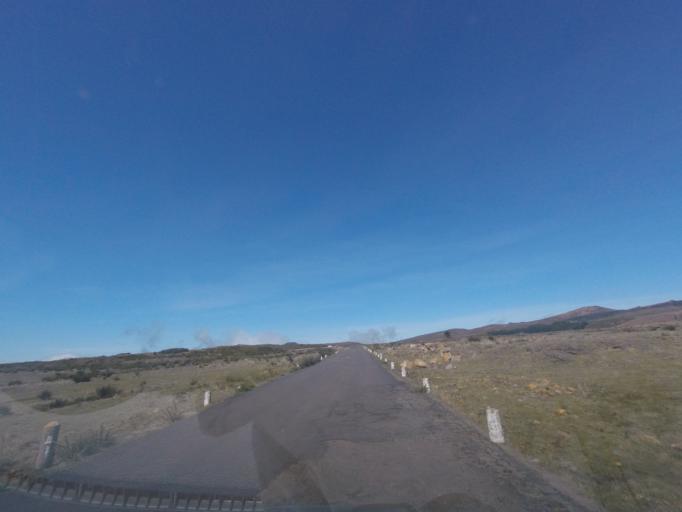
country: PT
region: Madeira
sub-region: Calheta
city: Arco da Calheta
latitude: 32.7447
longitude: -17.0975
